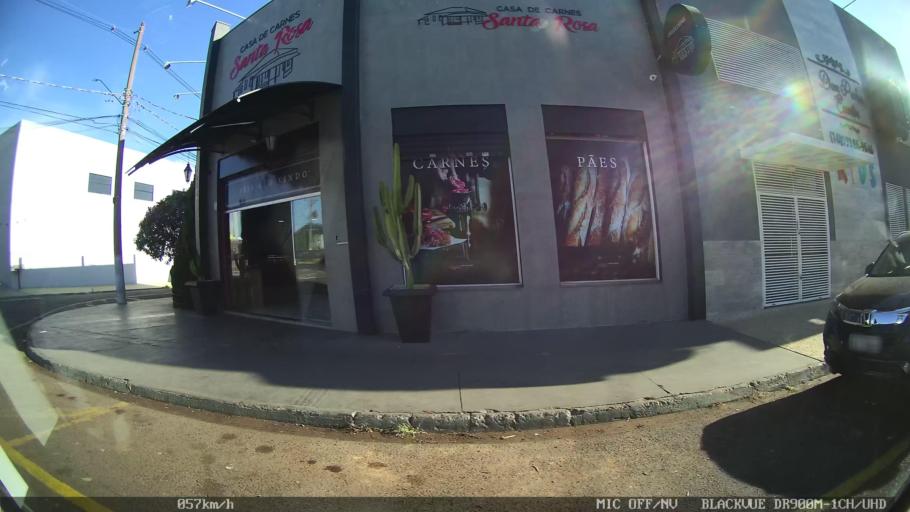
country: BR
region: Sao Paulo
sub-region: Franca
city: Franca
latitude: -20.5112
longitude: -47.3903
